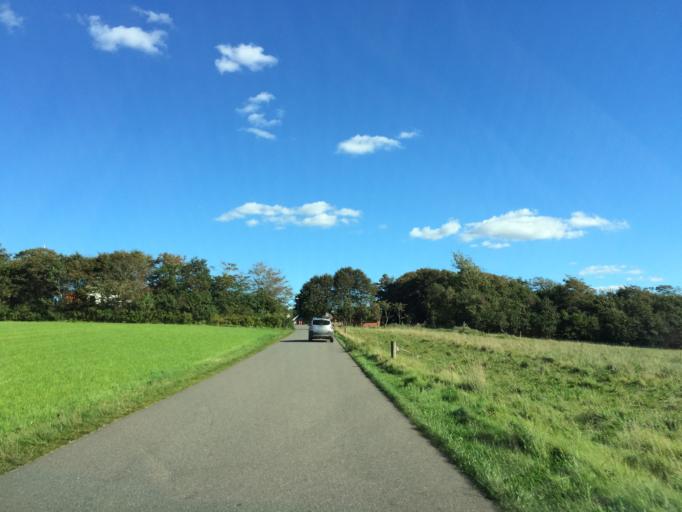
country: DK
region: Central Jutland
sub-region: Holstebro Kommune
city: Holstebro
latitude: 56.2623
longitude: 8.5429
